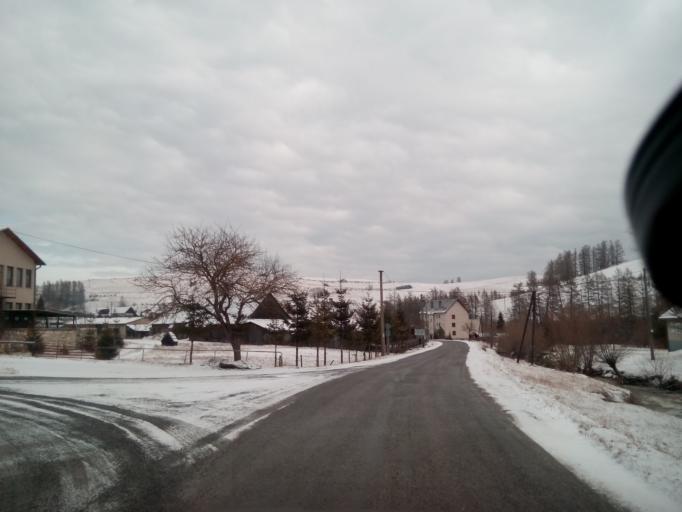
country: SK
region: Presovsky
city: Spisske Podhradie
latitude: 49.0824
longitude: 20.6984
